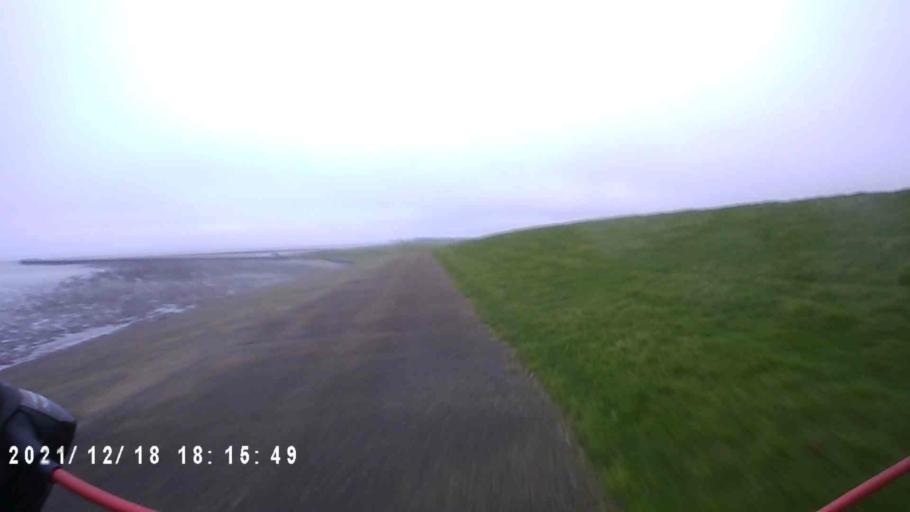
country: NL
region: Friesland
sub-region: Gemeente Dongeradeel
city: Ternaard
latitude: 53.3943
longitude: 5.9672
